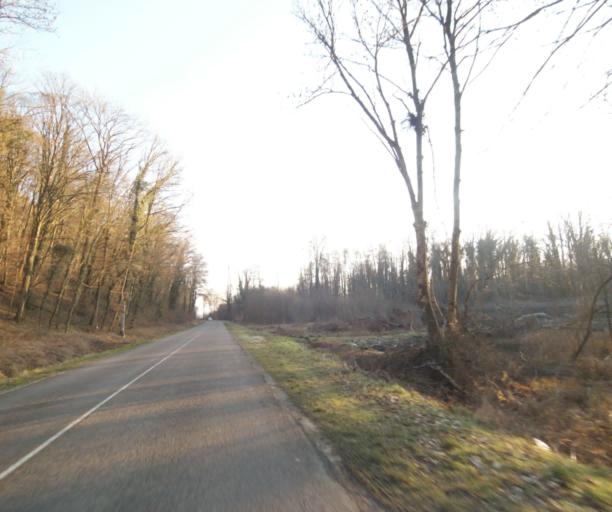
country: FR
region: Champagne-Ardenne
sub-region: Departement de la Haute-Marne
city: Chevillon
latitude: 48.5314
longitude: 5.1069
